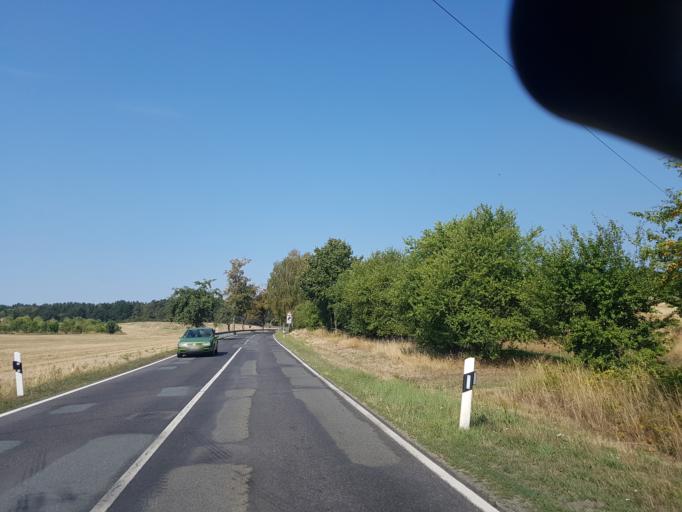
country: DE
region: Brandenburg
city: Belzig
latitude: 52.1316
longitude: 12.5355
